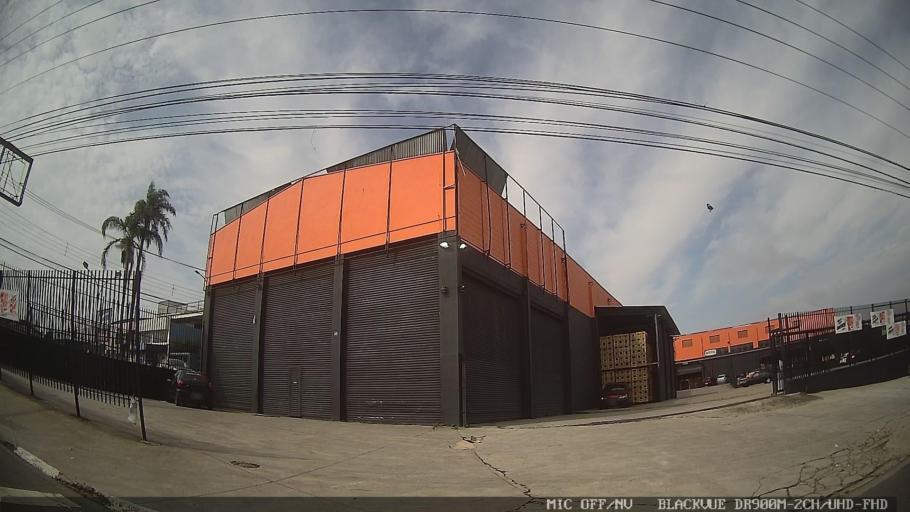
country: BR
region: Sao Paulo
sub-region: Jarinu
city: Jarinu
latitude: -23.1348
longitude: -46.7864
